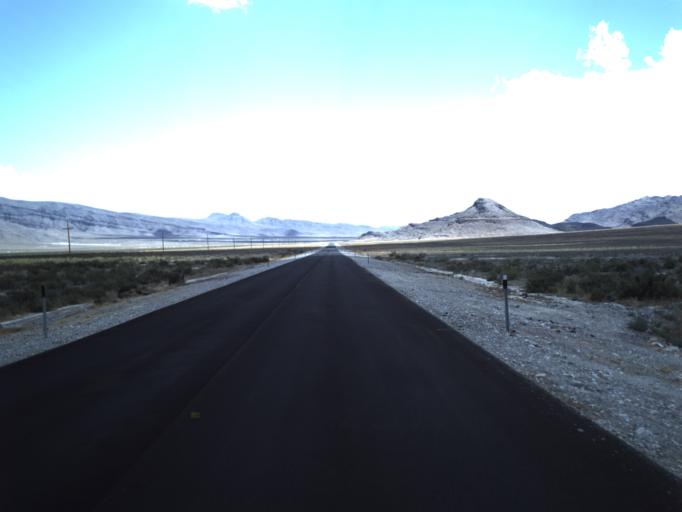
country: US
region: Utah
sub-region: Beaver County
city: Milford
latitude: 39.0785
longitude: -113.4829
